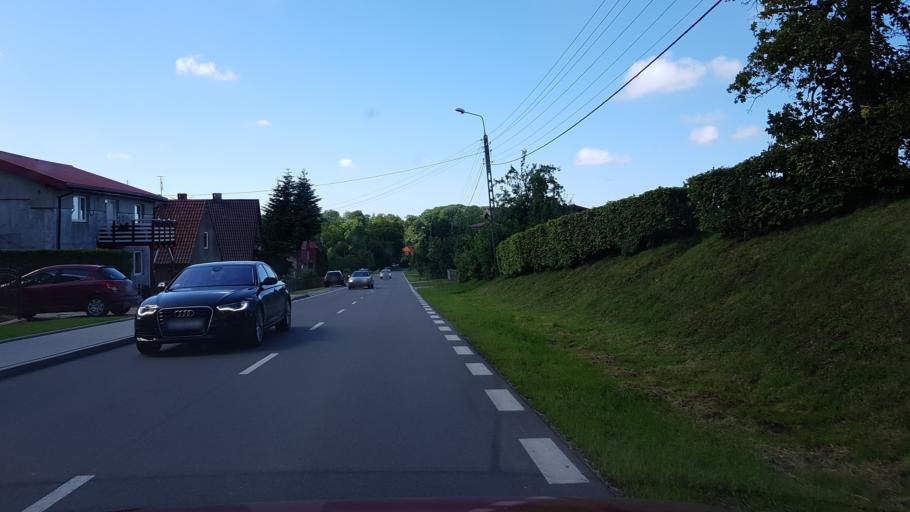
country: PL
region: West Pomeranian Voivodeship
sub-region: Powiat kolobrzeski
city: Ustronie Morskie
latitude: 54.1922
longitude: 15.9097
